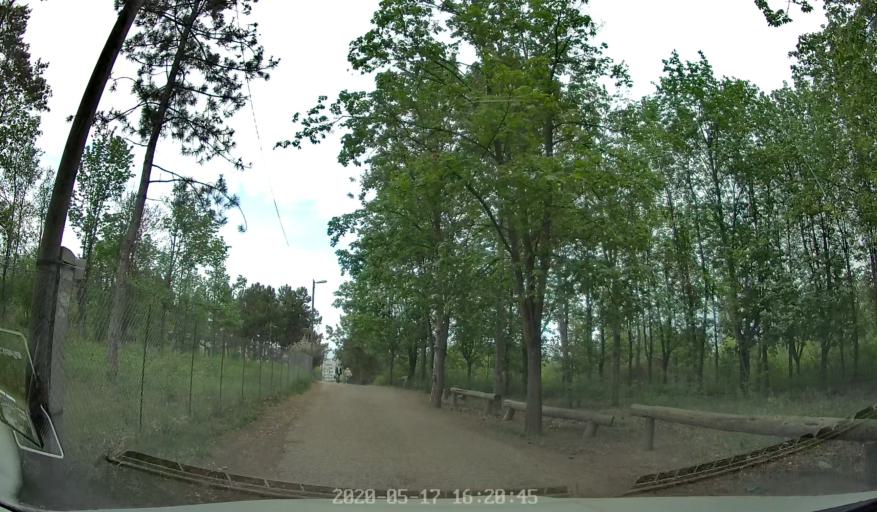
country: MD
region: Chisinau
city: Chisinau
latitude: 46.9727
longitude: 28.8747
